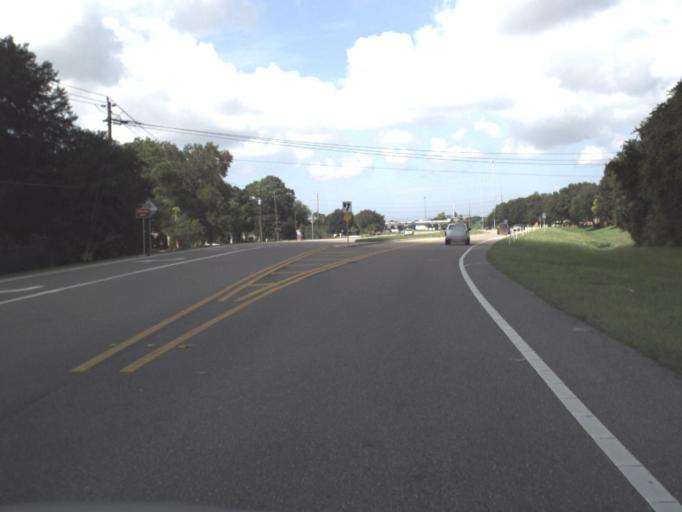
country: US
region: Florida
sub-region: Sarasota County
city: Lake Sarasota
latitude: 27.2691
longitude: -82.4412
